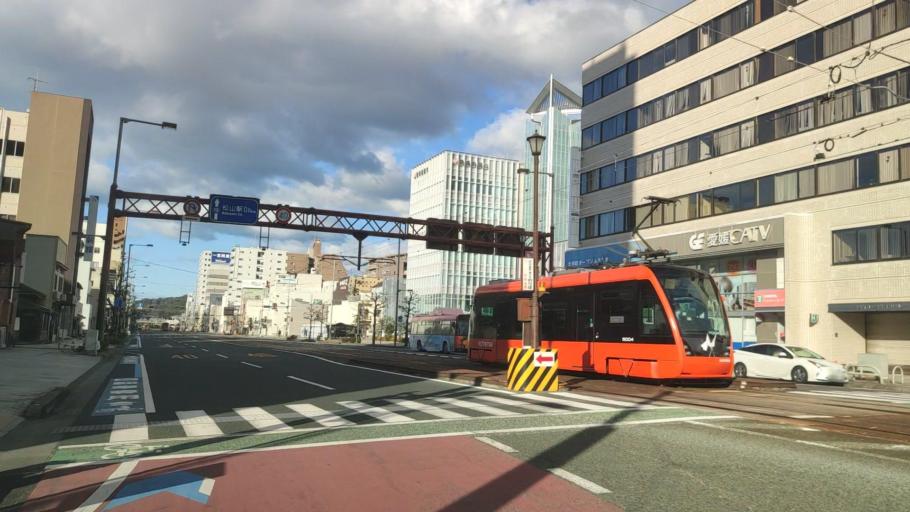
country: JP
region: Ehime
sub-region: Shikoku-chuo Shi
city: Matsuyama
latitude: 33.8400
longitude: 132.7585
